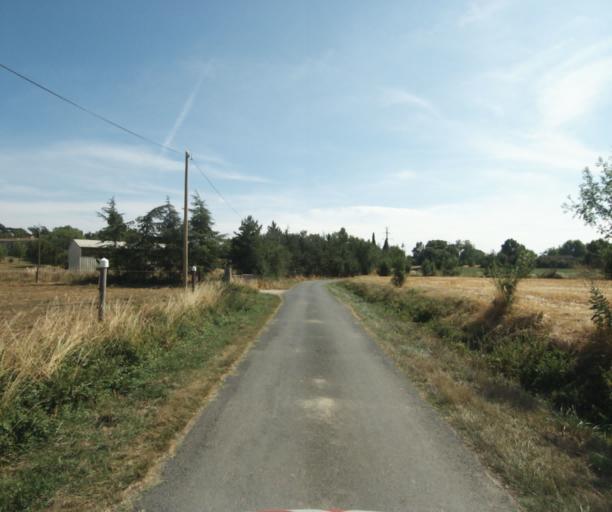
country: FR
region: Midi-Pyrenees
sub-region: Departement de la Haute-Garonne
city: Revel
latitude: 43.4891
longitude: 1.9906
